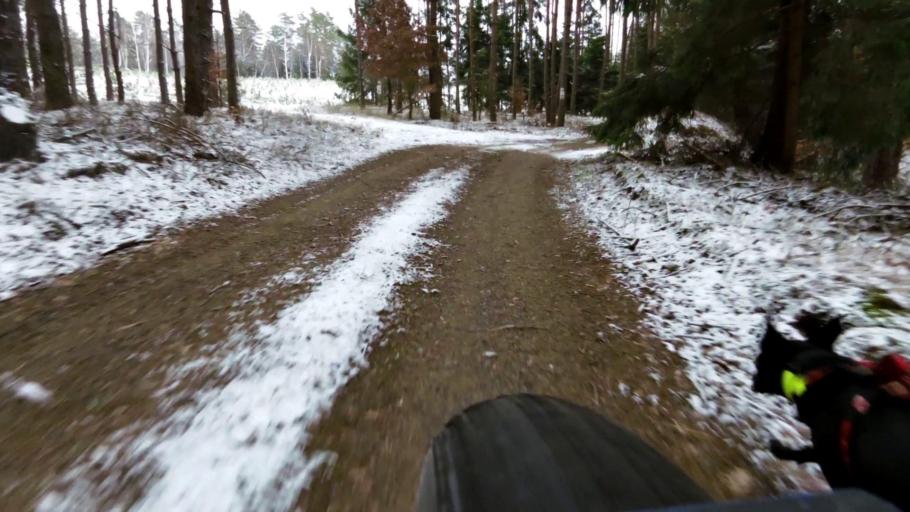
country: PL
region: West Pomeranian Voivodeship
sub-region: Powiat walecki
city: Miroslawiec
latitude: 53.3738
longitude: 16.1668
